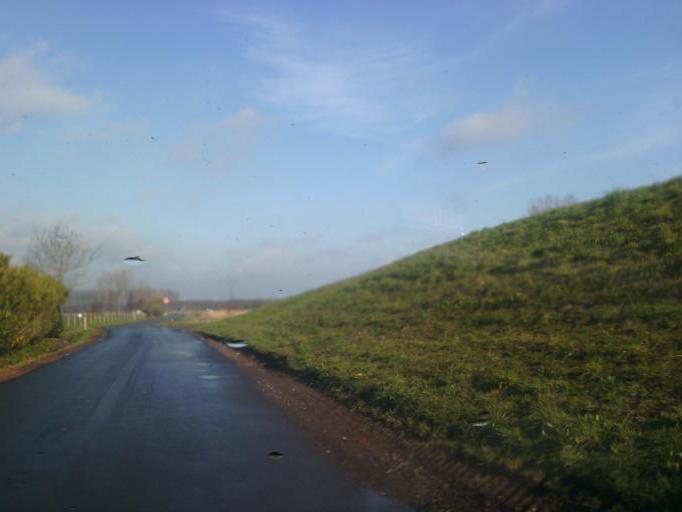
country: BE
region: Flanders
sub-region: Provincie Oost-Vlaanderen
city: Berlare
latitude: 51.0329
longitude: 4.0320
